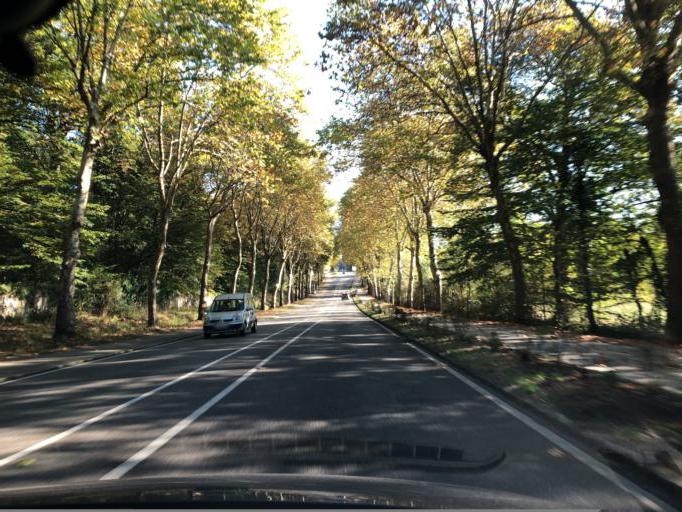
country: FR
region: Ile-de-France
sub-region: Departement des Yvelines
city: Rambouillet
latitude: 48.6600
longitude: 1.8274
